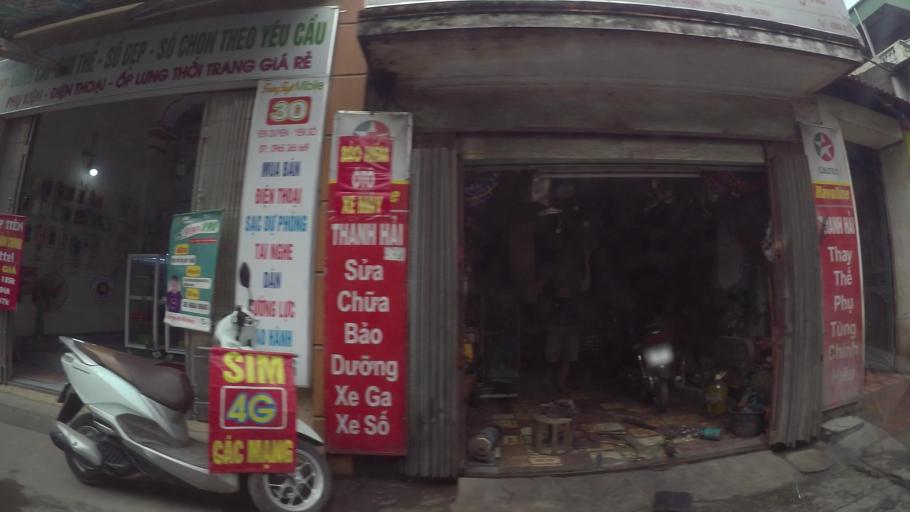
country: VN
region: Ha Noi
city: Van Dien
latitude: 20.9731
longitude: 105.8678
